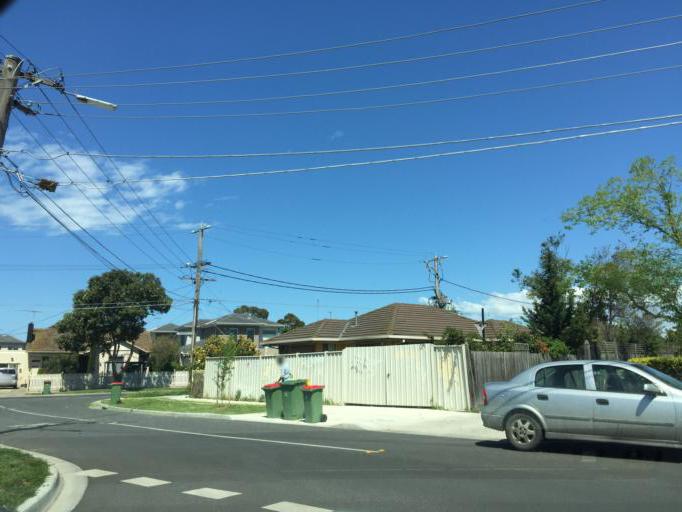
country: AU
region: Victoria
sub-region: Maribyrnong
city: Braybrook
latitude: -37.7842
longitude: 144.8544
